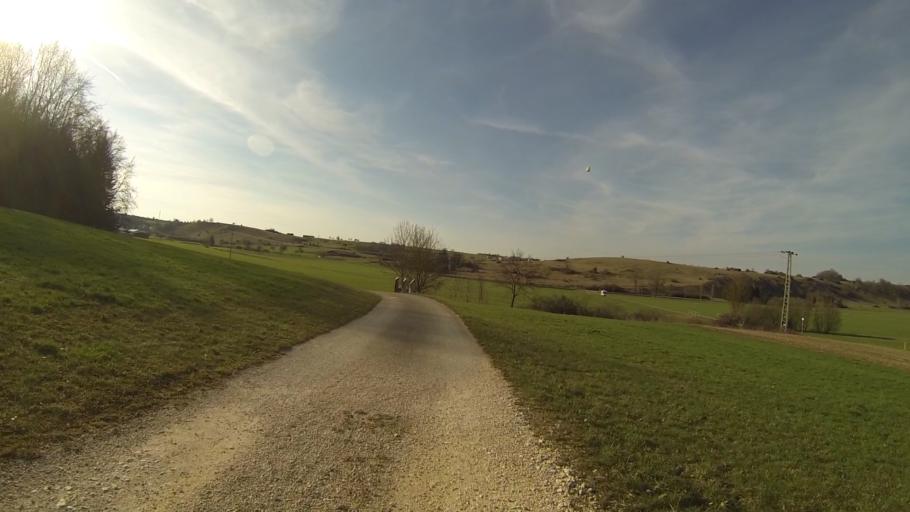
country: DE
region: Baden-Wuerttemberg
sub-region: Regierungsbezirk Stuttgart
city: Giengen an der Brenz
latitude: 48.5949
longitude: 10.2189
